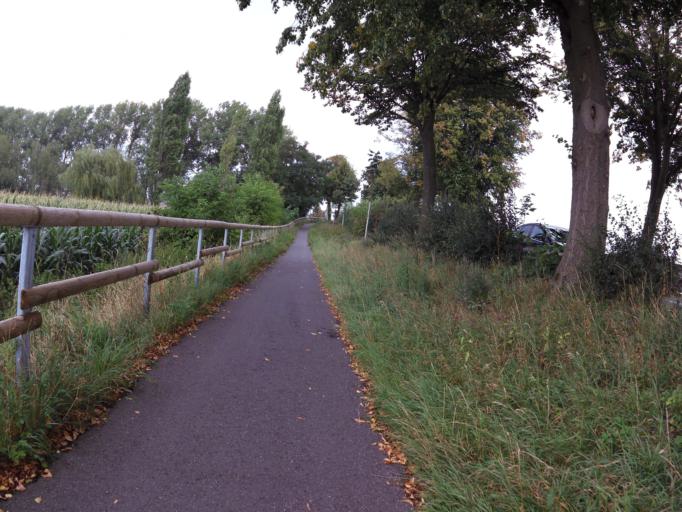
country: DE
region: Lower Saxony
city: Blender
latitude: 52.9245
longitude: 9.1731
